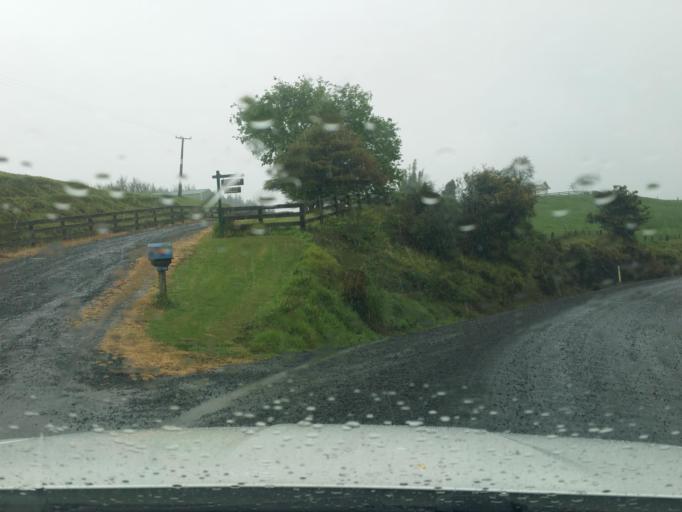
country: NZ
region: Northland
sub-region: Kaipara District
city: Dargaville
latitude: -35.8228
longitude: 174.0060
